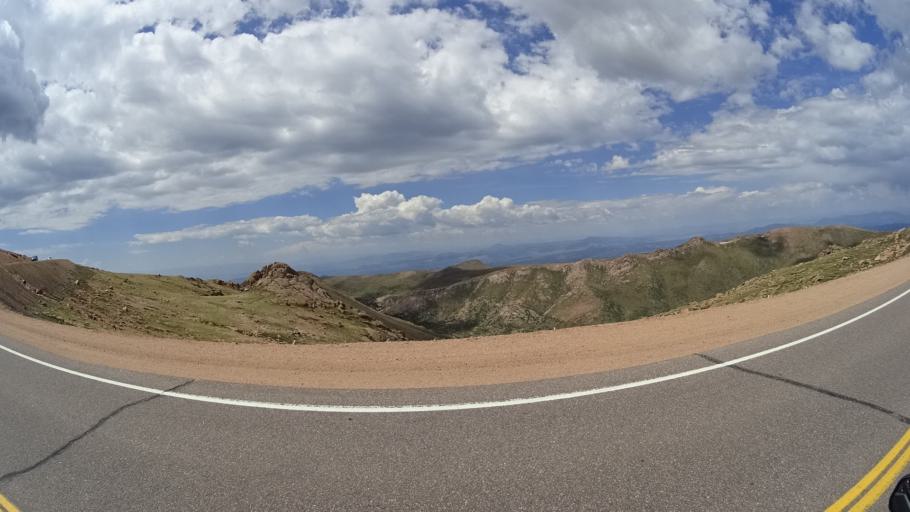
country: US
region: Colorado
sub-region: El Paso County
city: Cascade-Chipita Park
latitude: 38.8515
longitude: -105.0614
